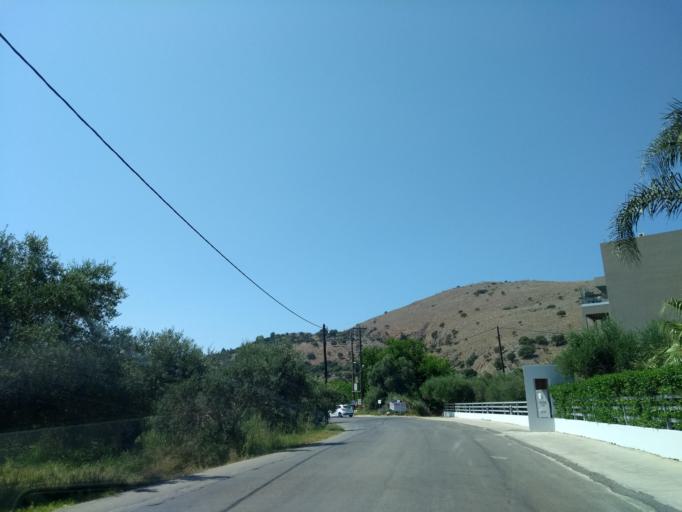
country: GR
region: Crete
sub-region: Nomos Chanias
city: Georgioupolis
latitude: 35.3657
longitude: 24.2568
